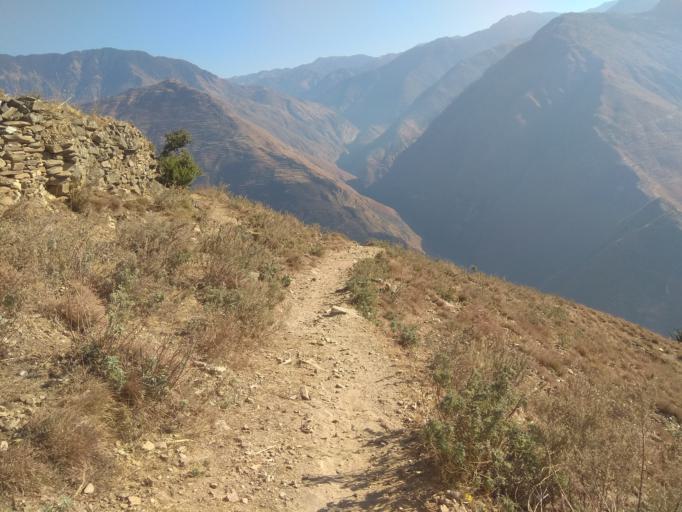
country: NP
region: Mid Western
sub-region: Karnali Zone
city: Jumla
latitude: 29.3124
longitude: 81.7416
